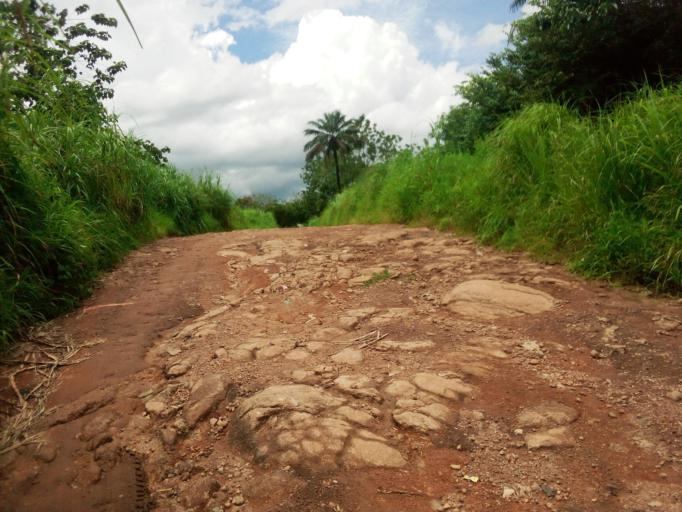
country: SL
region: Eastern Province
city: Simbakoro
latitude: 8.6071
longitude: -10.9847
